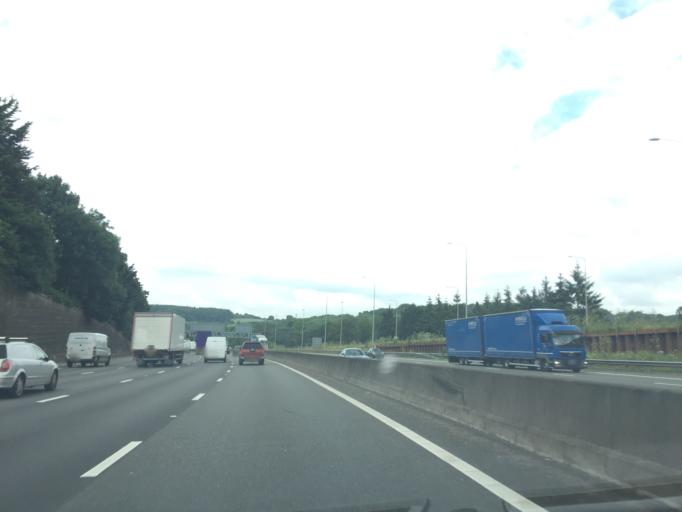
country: GB
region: England
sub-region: Hertfordshire
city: Chorleywood
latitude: 51.6565
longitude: -0.4944
